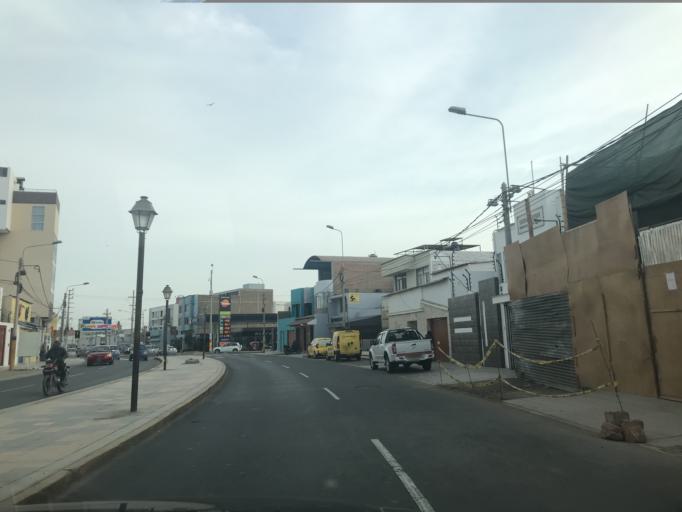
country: PE
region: Lambayeque
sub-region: Provincia de Chiclayo
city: Chiclayo
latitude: -6.7874
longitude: -79.8446
